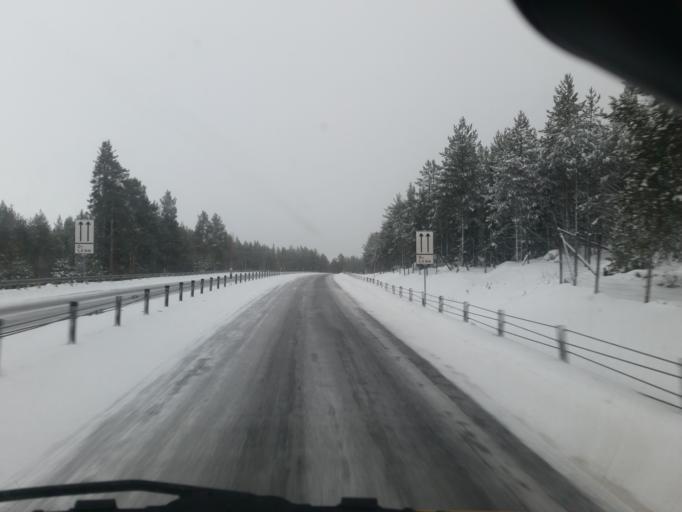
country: SE
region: Norrbotten
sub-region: Pitea Kommun
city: Pitea
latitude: 65.1241
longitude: 21.5249
